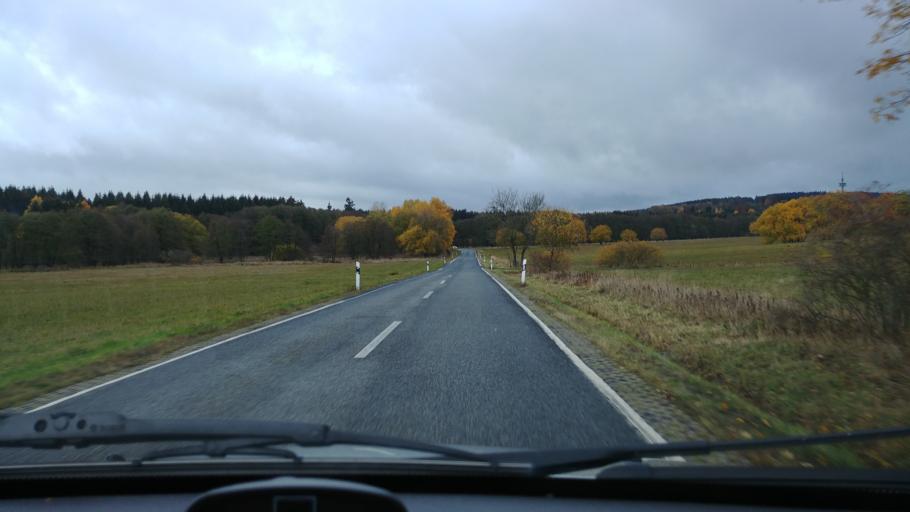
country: DE
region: Hesse
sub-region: Regierungsbezirk Giessen
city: Driedorf
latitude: 50.6588
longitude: 8.1827
